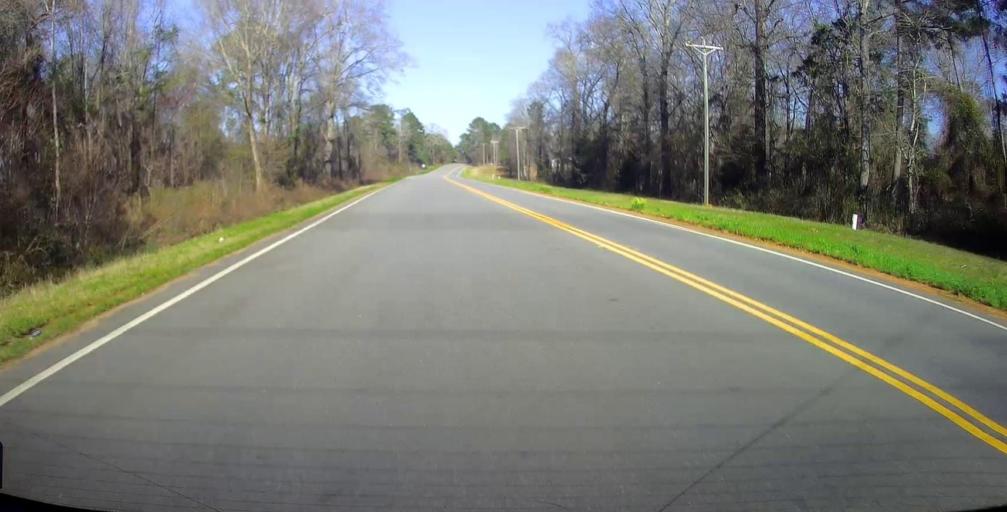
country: US
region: Georgia
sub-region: Macon County
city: Montezuma
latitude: 32.3166
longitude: -83.8950
